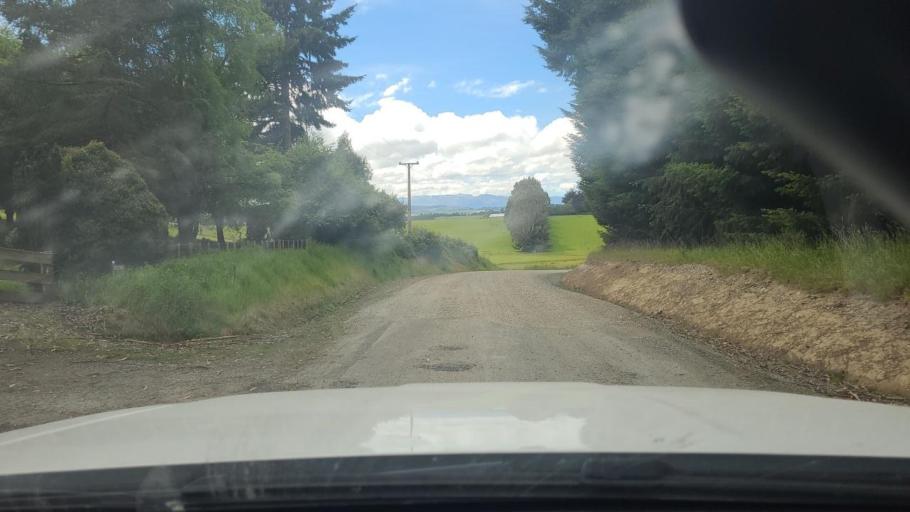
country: NZ
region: Southland
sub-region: Southland District
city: Te Anau
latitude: -45.4859
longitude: 167.8066
